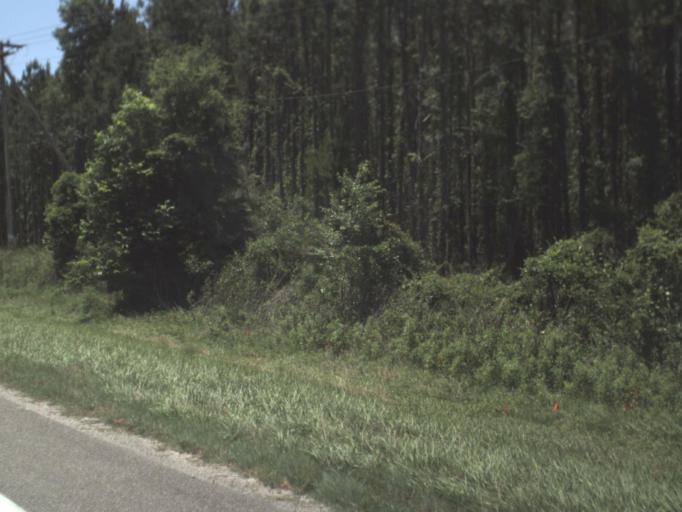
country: US
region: Florida
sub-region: Lafayette County
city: Mayo
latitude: 29.9502
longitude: -82.9492
